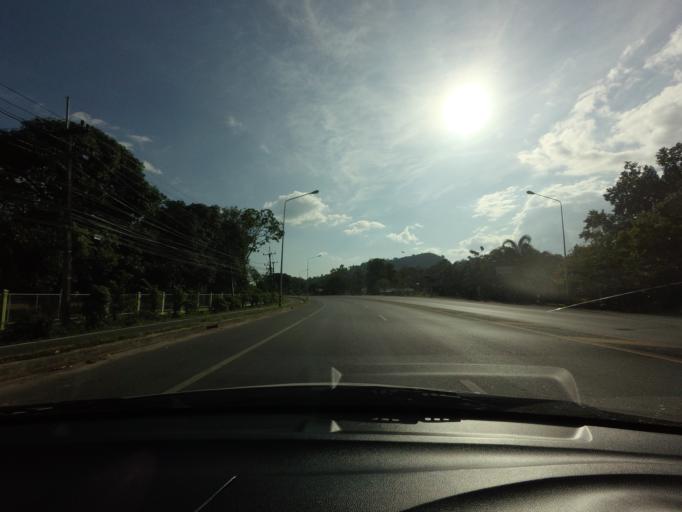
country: TH
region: Nakhon Nayok
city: Nakhon Nayok
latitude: 14.3081
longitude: 101.2937
